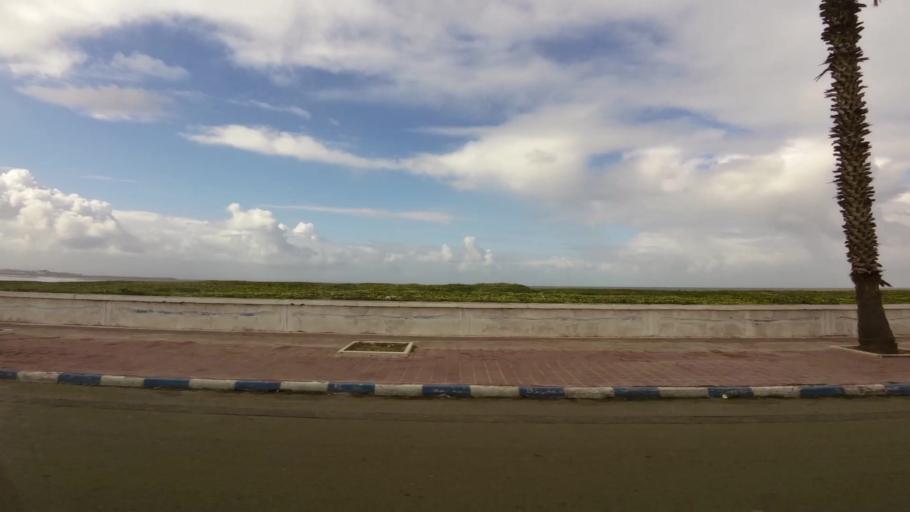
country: MA
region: Doukkala-Abda
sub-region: El-Jadida
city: El Jadida
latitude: 33.2442
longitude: -8.4856
